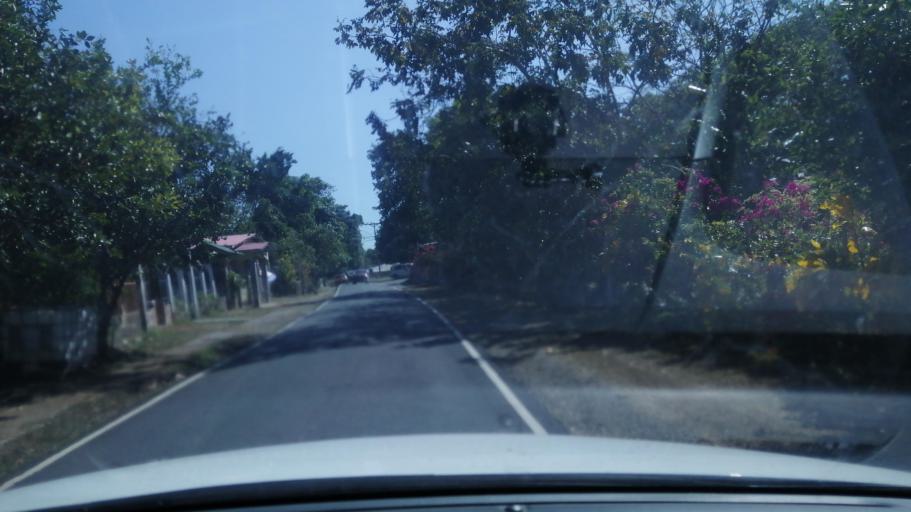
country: PA
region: Chiriqui
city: San Felix
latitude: 8.2906
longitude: -81.8711
